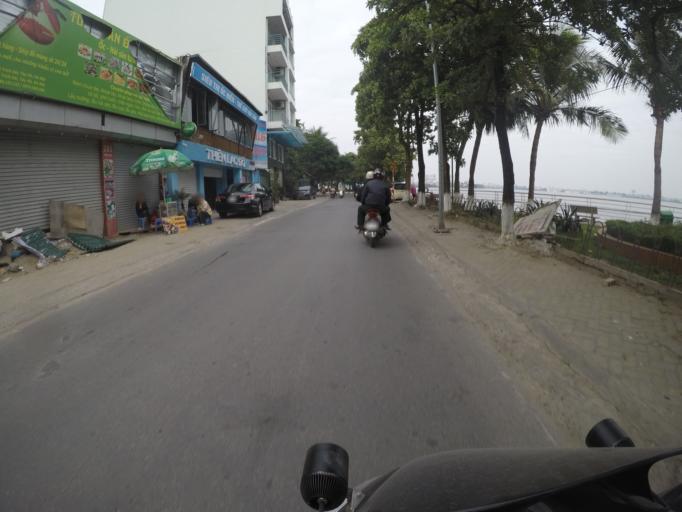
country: VN
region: Ha Noi
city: Cau Giay
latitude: 21.0475
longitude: 105.8143
